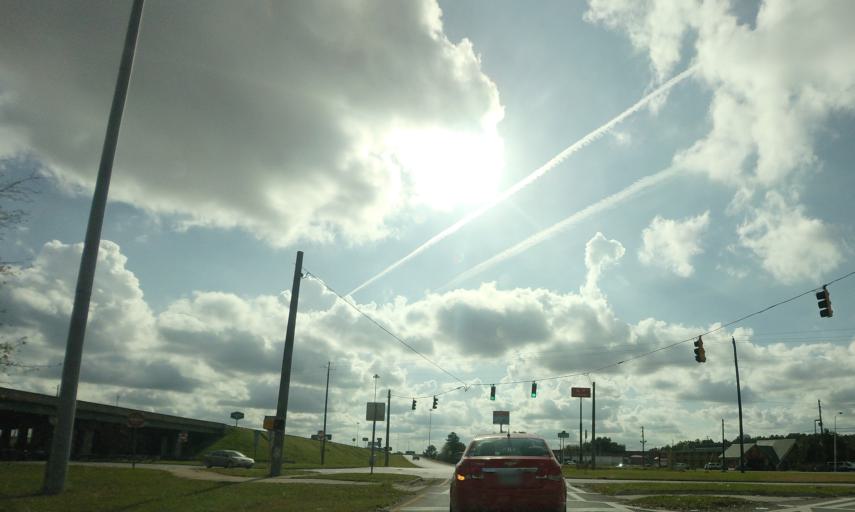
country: US
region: Georgia
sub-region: Houston County
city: Perry
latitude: 32.4724
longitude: -83.7442
